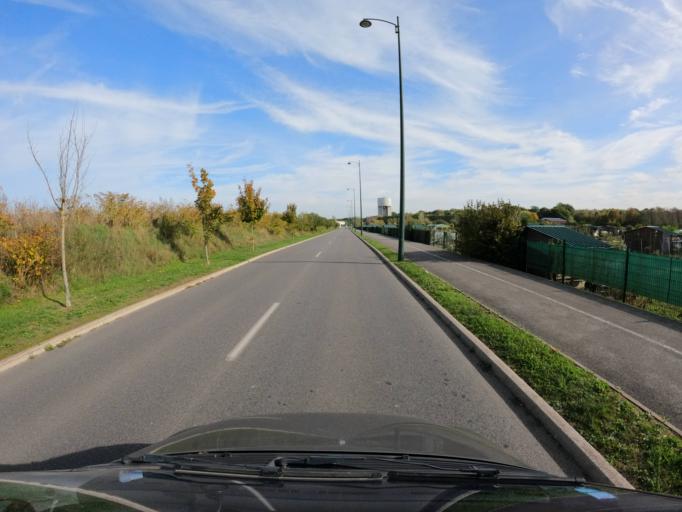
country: FR
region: Ile-de-France
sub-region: Departement du Val-de-Marne
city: La Queue-en-Brie
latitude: 48.7754
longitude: 2.5880
